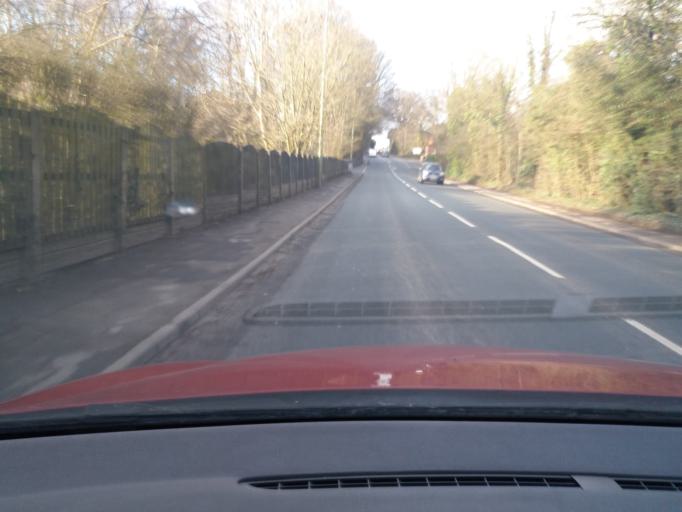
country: GB
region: England
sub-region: Lancashire
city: Euxton
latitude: 53.6555
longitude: -2.6752
